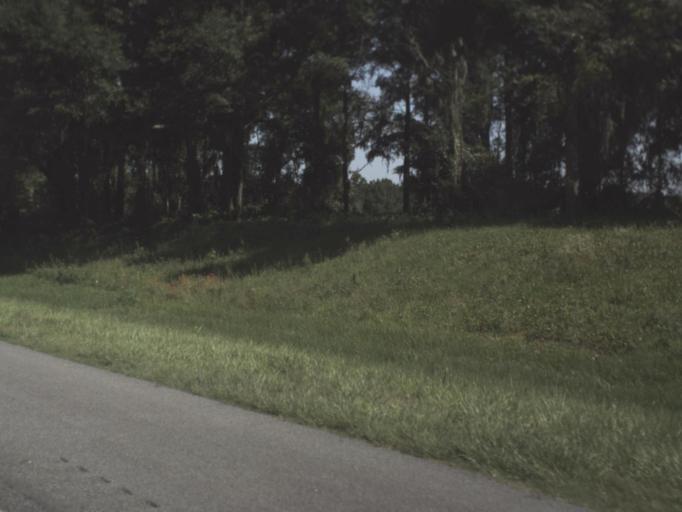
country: US
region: Florida
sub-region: Suwannee County
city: Live Oak
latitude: 30.3381
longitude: -82.9726
